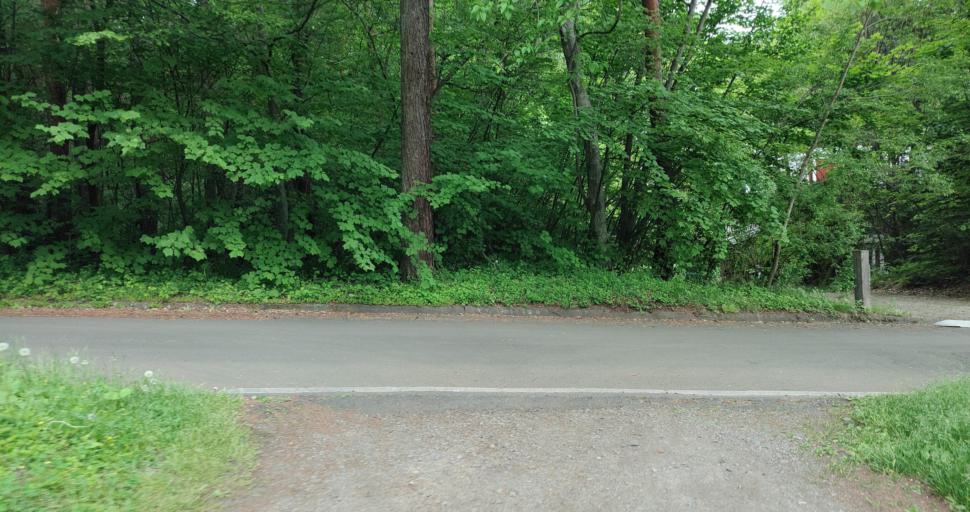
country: JP
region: Nagano
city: Komoro
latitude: 36.3421
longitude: 138.4642
